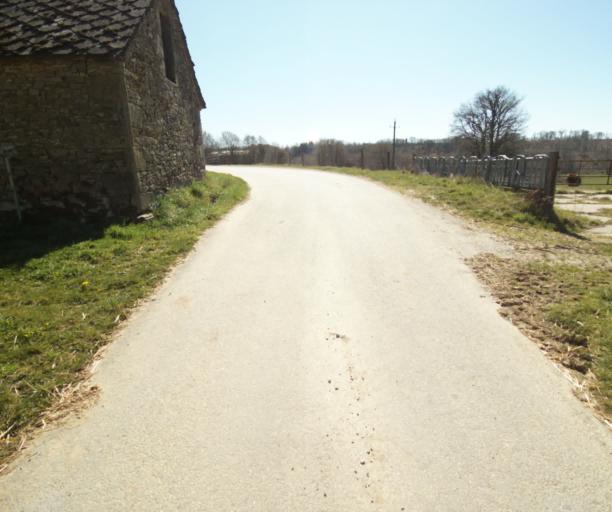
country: FR
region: Limousin
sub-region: Departement de la Correze
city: Chamboulive
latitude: 45.4571
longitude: 1.7020
